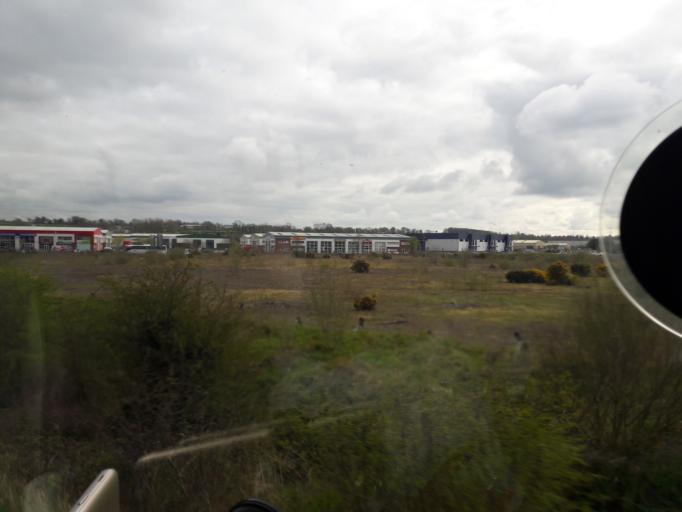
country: IE
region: Leinster
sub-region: An Longfort
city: Longford
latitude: 53.7232
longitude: -7.8099
